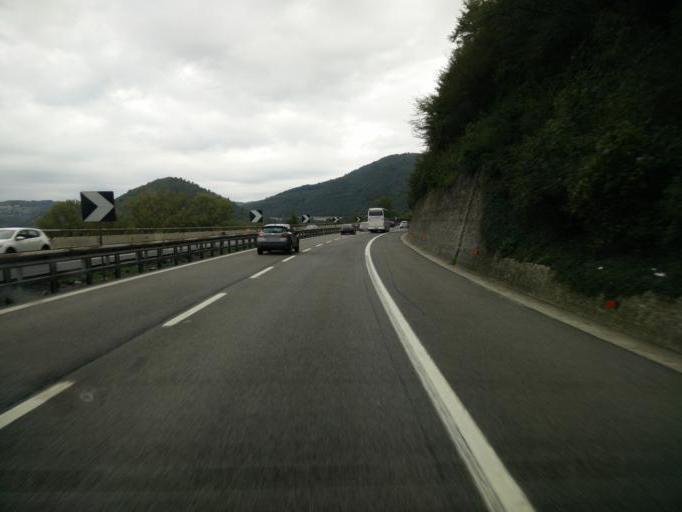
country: IT
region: Tuscany
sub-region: Province of Florence
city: Carraia
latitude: 43.9180
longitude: 11.2015
